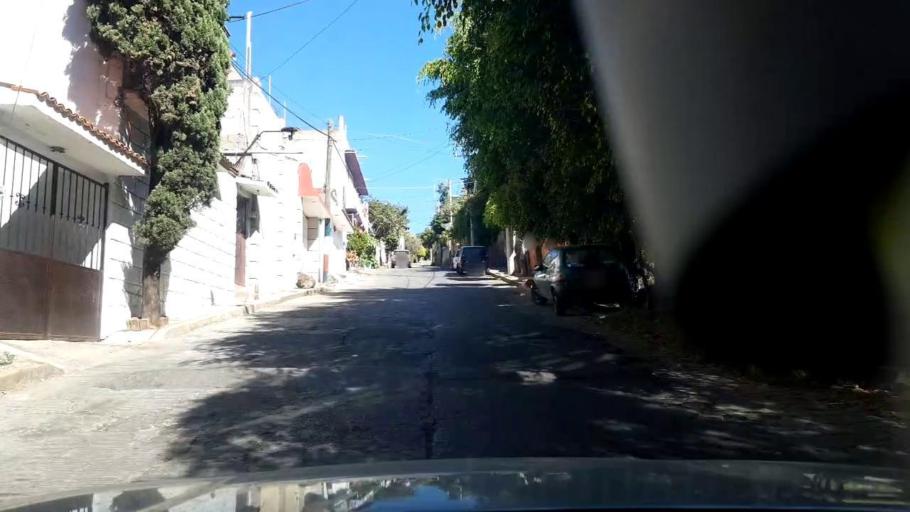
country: MX
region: Morelos
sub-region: Cuernavaca
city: Lomas de Ahuatepec
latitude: 18.9730
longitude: -99.2136
